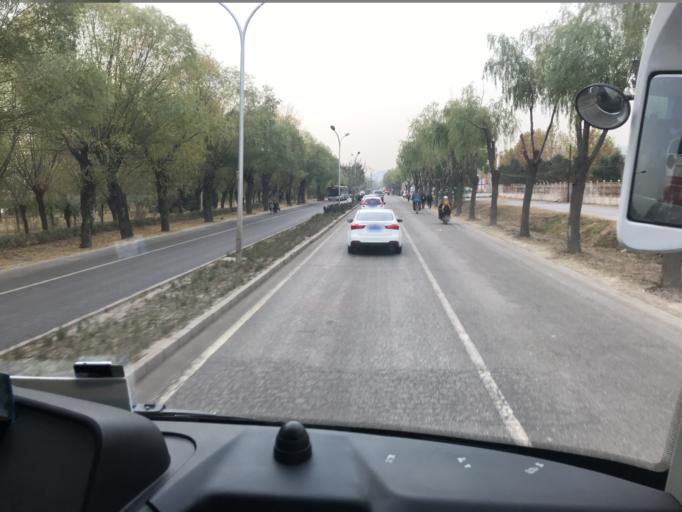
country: CN
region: Beijing
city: Wenquan
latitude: 40.0901
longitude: 116.2097
